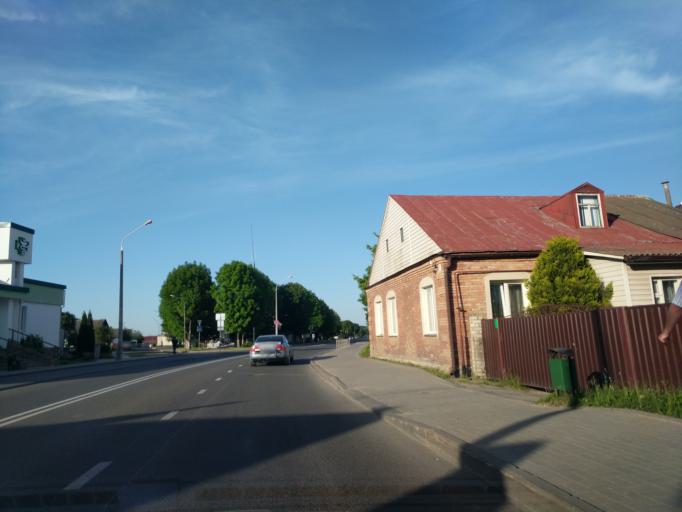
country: BY
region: Grodnenskaya
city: Ashmyany
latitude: 54.4277
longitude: 25.9424
